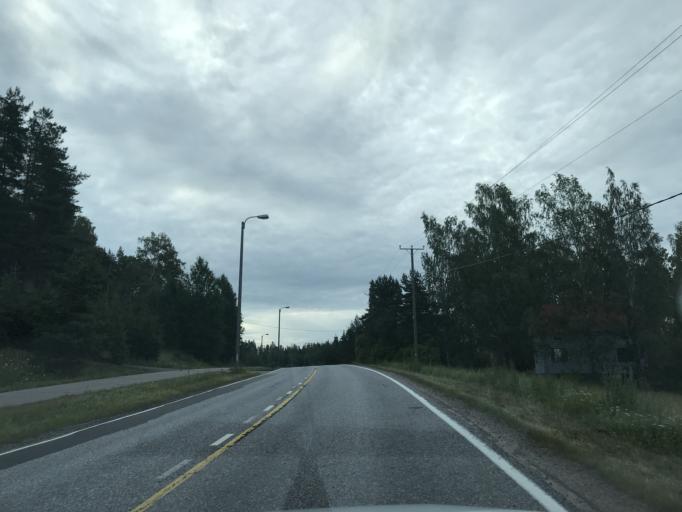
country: FI
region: Uusimaa
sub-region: Helsinki
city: Nurmijaervi
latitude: 60.3814
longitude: 24.6661
